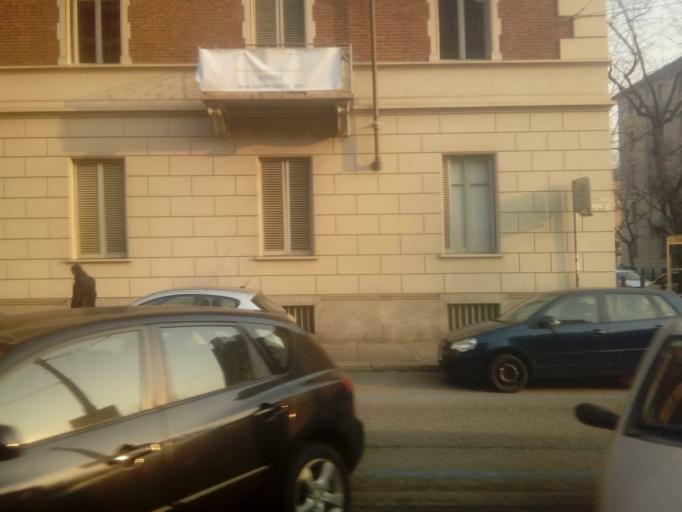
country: IT
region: Piedmont
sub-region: Provincia di Torino
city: Turin
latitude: 45.0595
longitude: 7.6635
